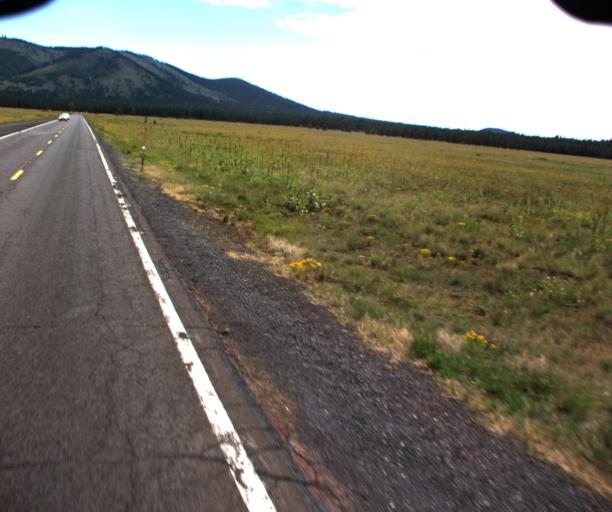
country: US
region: Arizona
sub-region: Coconino County
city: Flagstaff
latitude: 35.4133
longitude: -111.7557
